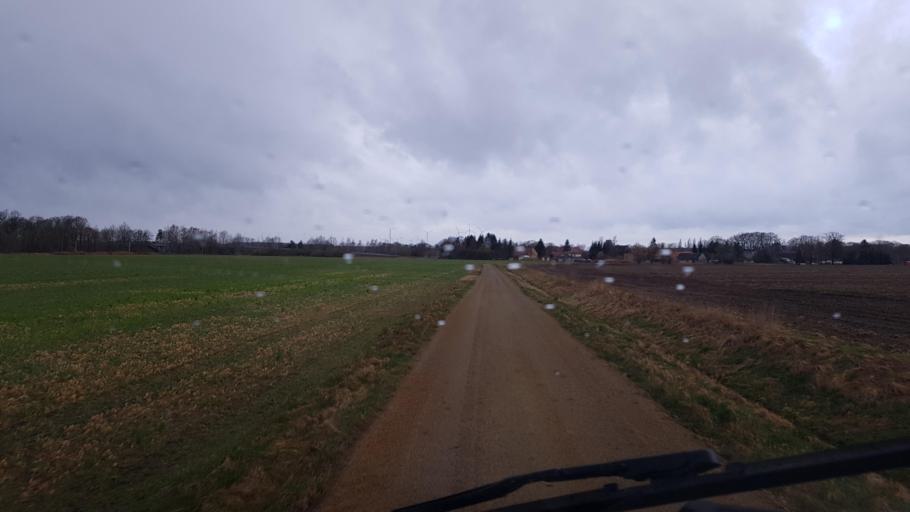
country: DE
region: Brandenburg
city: Bronkow
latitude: 51.6436
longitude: 13.9351
